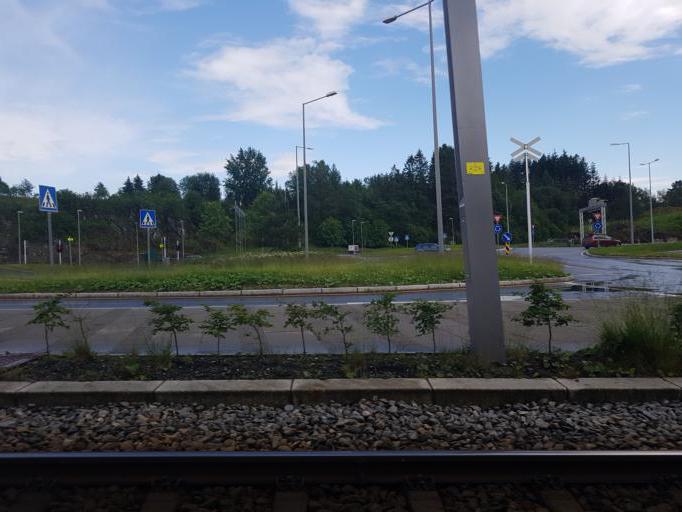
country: NO
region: Hordaland
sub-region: Bergen
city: Ytrebygda
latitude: 60.2878
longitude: 5.2612
